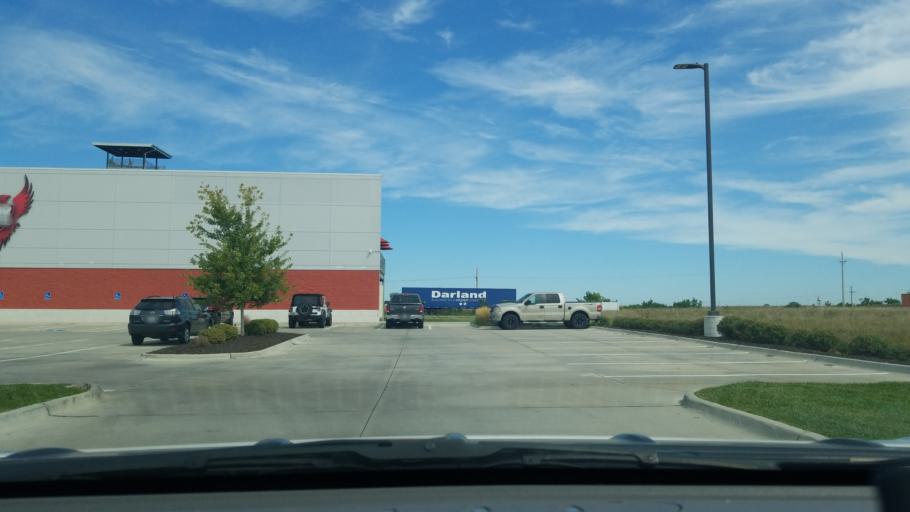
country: US
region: Nebraska
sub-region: Sarpy County
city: Chalco
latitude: 41.1456
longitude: -96.1551
